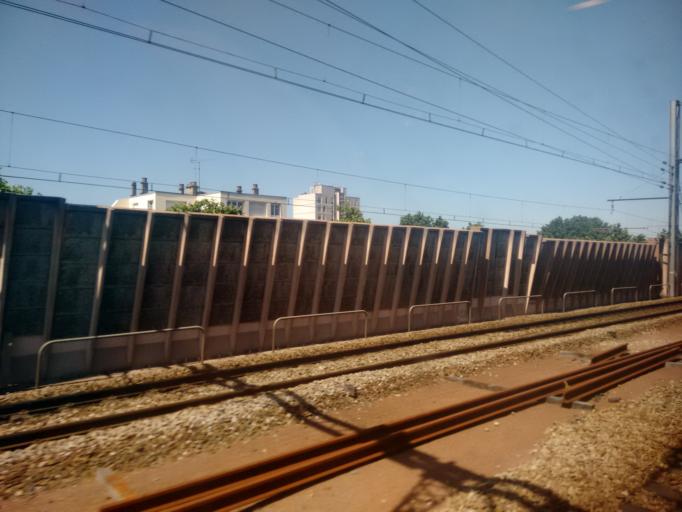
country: FR
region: Ile-de-France
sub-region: Departement des Hauts-de-Seine
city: Malakoff
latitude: 48.8154
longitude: 2.2966
